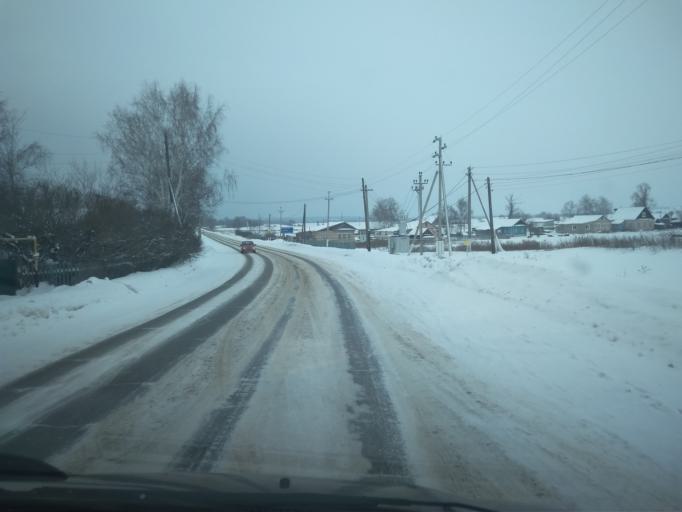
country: RU
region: Mordoviya
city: Kemlya
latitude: 54.6921
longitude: 45.2793
